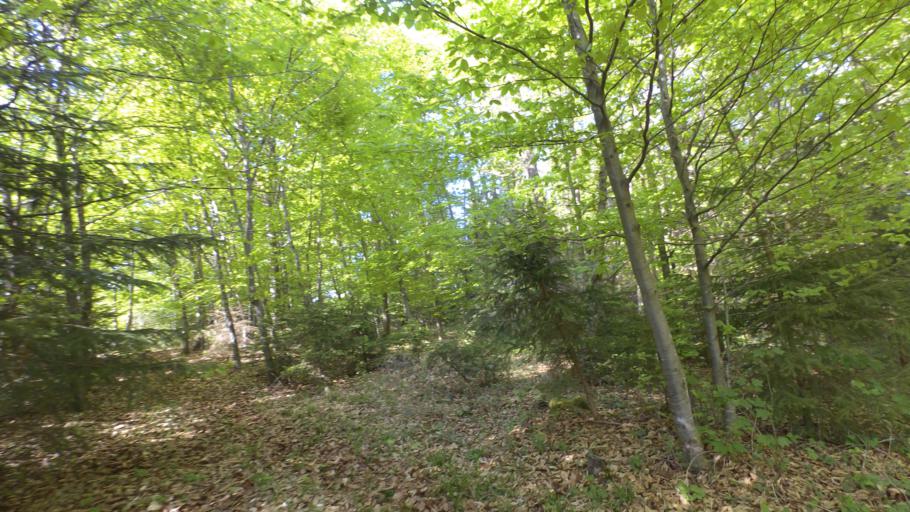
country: DE
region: Bavaria
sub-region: Upper Bavaria
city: Chieming
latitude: 47.9418
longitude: 12.5384
